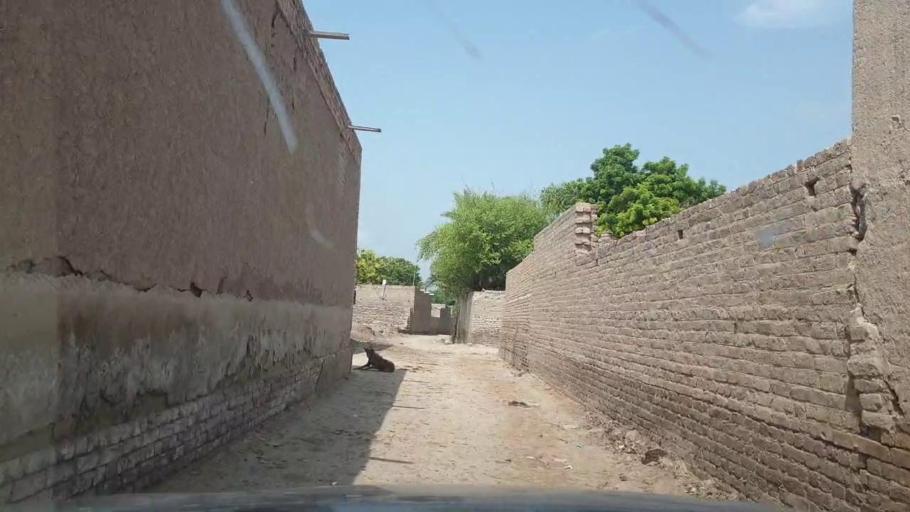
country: PK
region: Sindh
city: Ratodero
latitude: 27.8624
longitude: 68.3099
